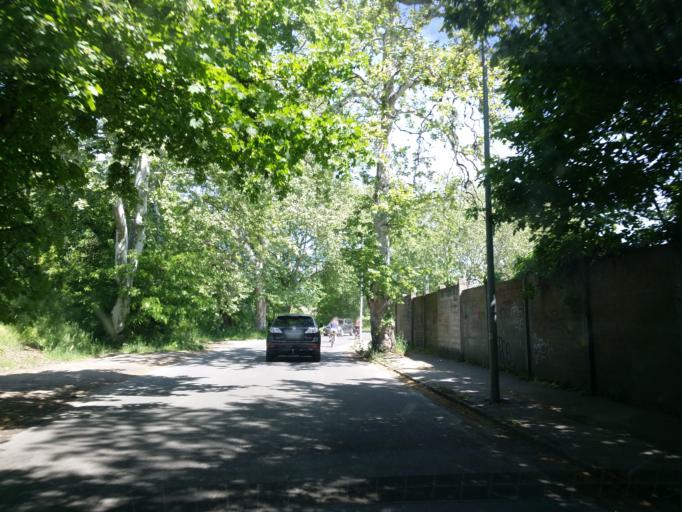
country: HU
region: Budapest
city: Budapest III. keruelet
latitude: 47.5641
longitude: 19.0545
